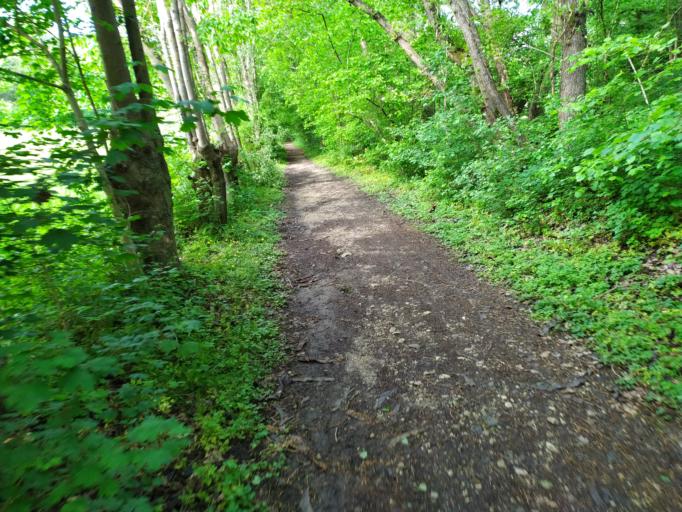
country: IT
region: Veneto
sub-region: Provincia di Vicenza
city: Sarcedo
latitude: 45.7061
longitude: 11.5206
